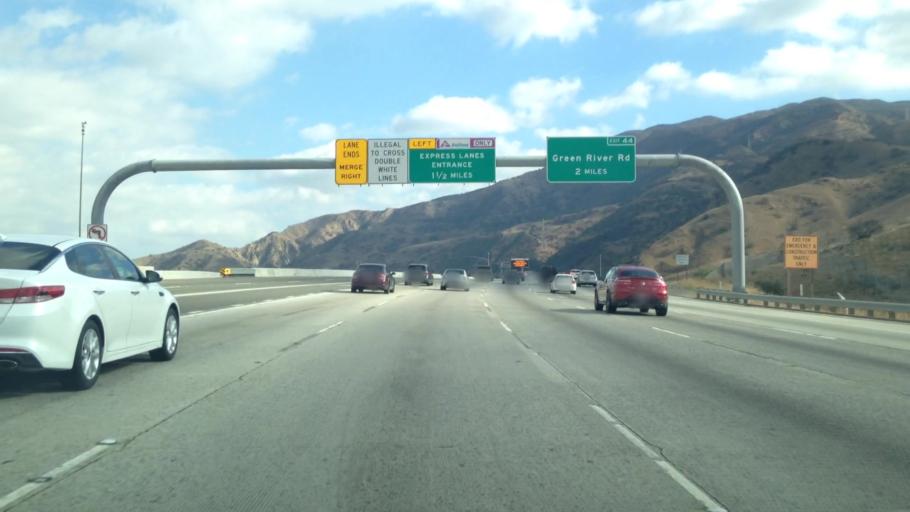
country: US
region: California
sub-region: San Bernardino County
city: Los Serranos
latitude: 33.8733
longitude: -117.6912
